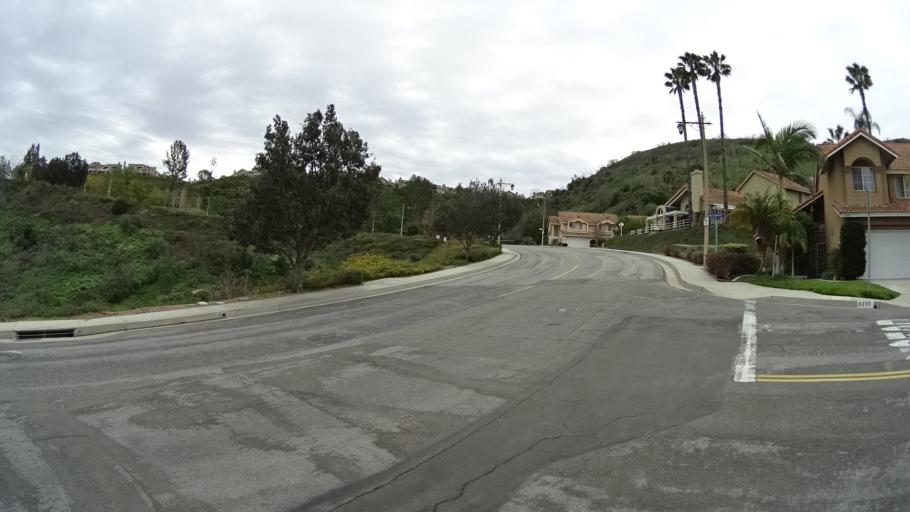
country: US
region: California
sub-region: Orange County
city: Villa Park
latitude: 33.8363
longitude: -117.7784
